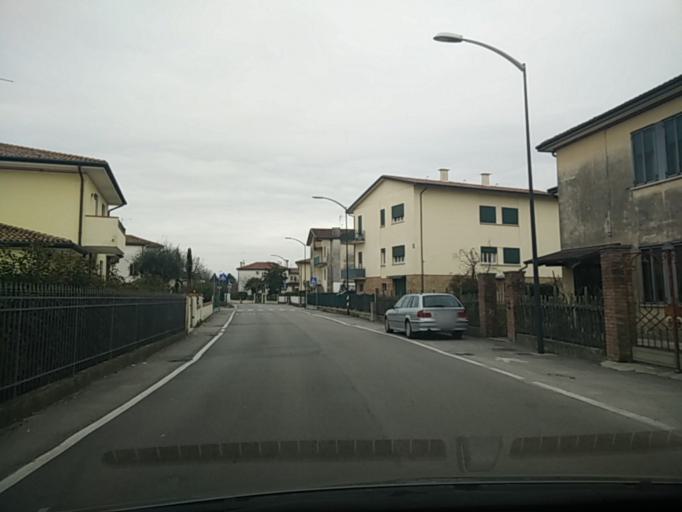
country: IT
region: Veneto
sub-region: Provincia di Treviso
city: Treviso
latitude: 45.6547
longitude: 12.2241
